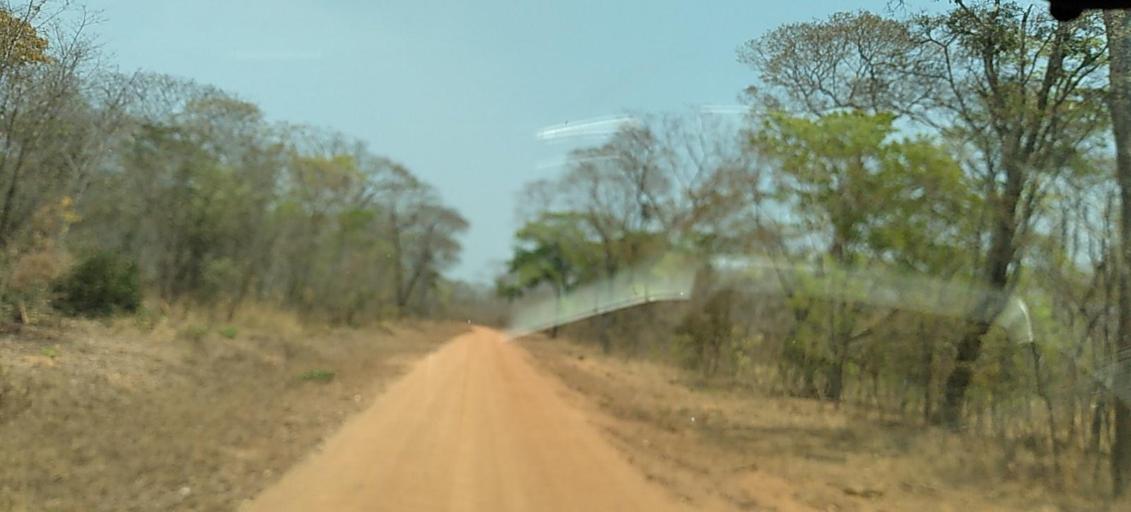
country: ZM
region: Central
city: Mumbwa
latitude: -14.3749
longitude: 26.4805
